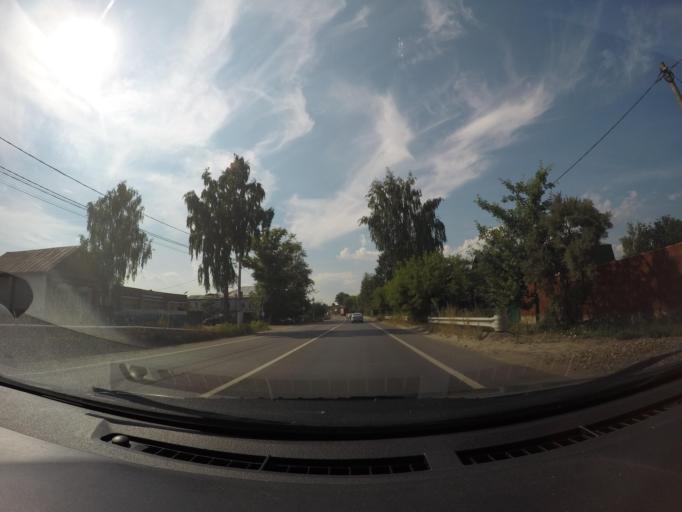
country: RU
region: Moskovskaya
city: Rechitsy
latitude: 55.5981
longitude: 38.4657
